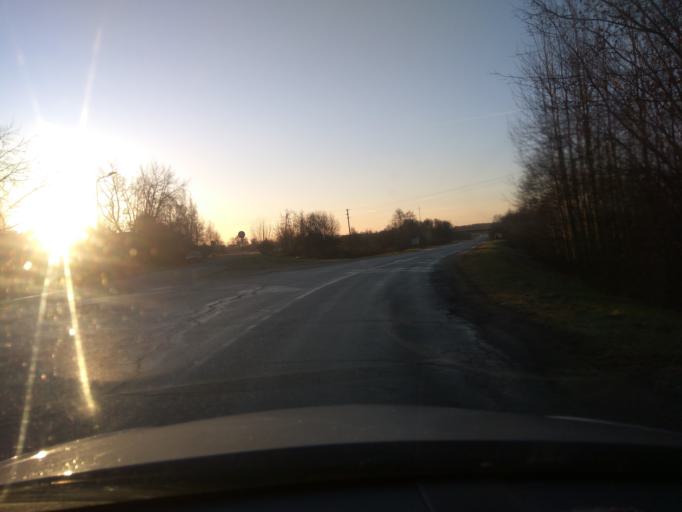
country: LV
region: Kuldigas Rajons
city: Kuldiga
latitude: 56.9664
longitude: 22.0030
